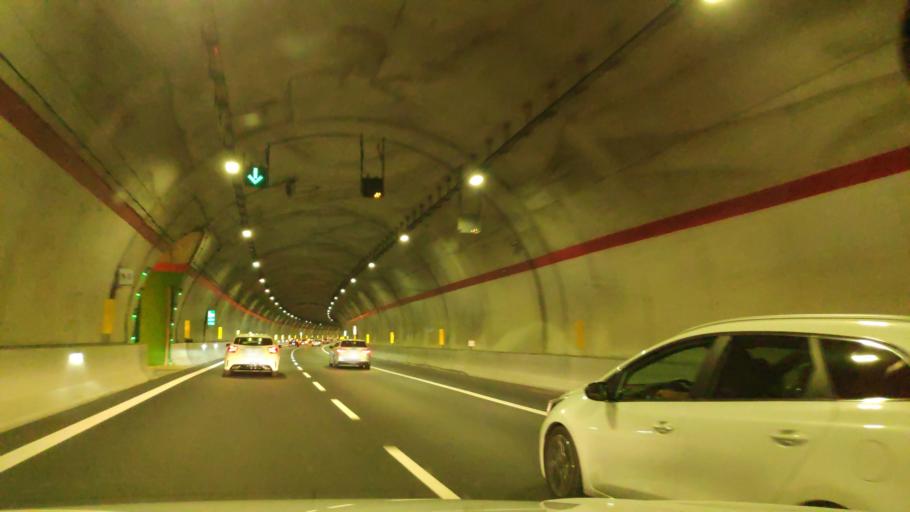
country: IT
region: Calabria
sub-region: Provincia di Cosenza
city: Mormanno
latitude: 39.8875
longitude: 15.9823
